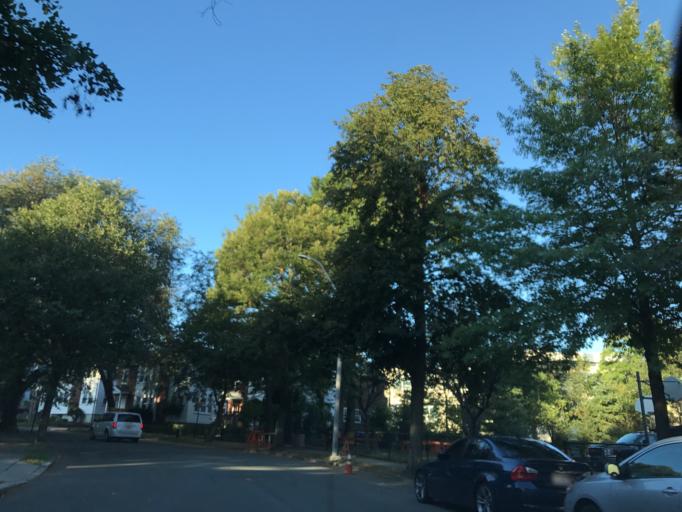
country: US
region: Massachusetts
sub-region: Norfolk County
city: Brookline
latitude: 42.3497
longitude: -71.1268
